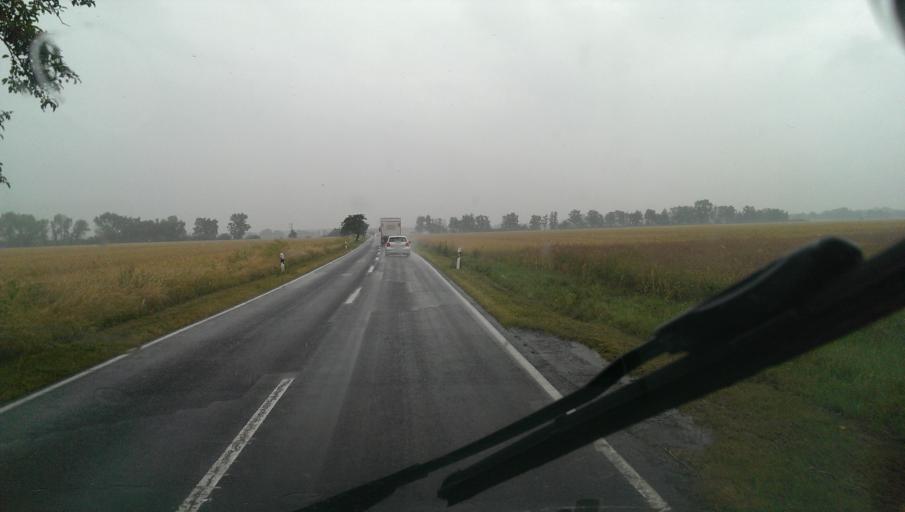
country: DE
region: Brandenburg
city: Roskow
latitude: 52.4694
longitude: 12.6891
